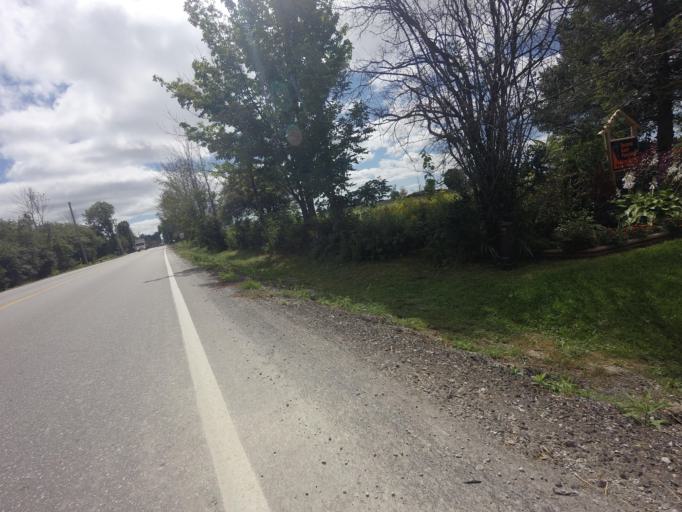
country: CA
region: Ontario
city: Uxbridge
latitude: 44.1277
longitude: -79.1553
